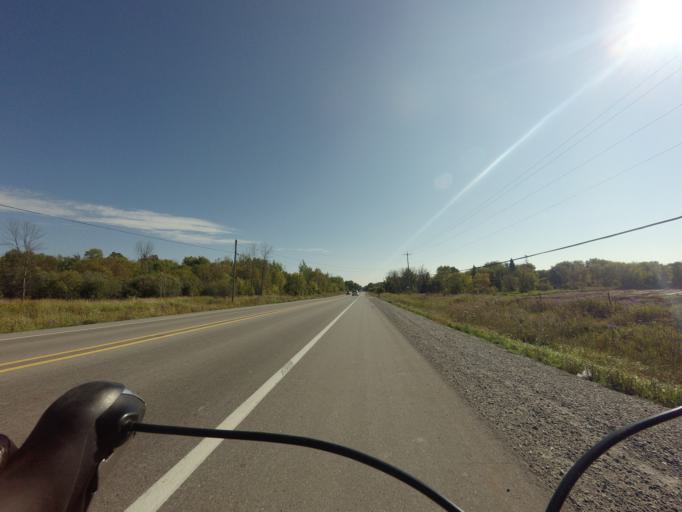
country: CA
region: Ontario
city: Bells Corners
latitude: 45.2608
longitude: -75.7001
